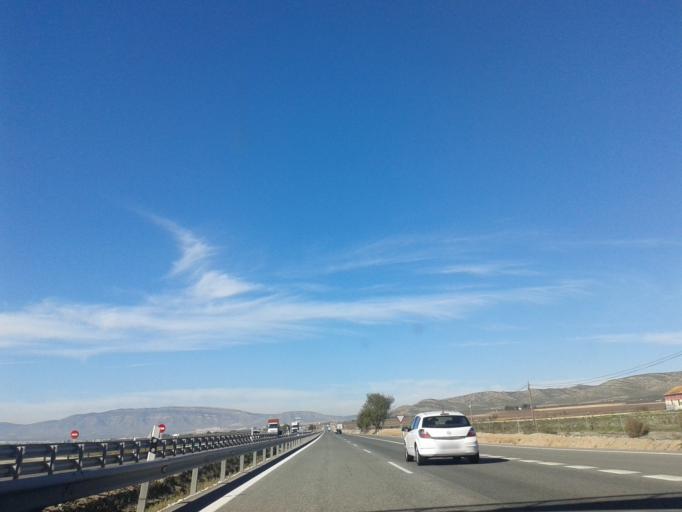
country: ES
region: Valencia
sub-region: Provincia de Alicante
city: Villena
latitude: 38.6725
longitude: -0.8883
